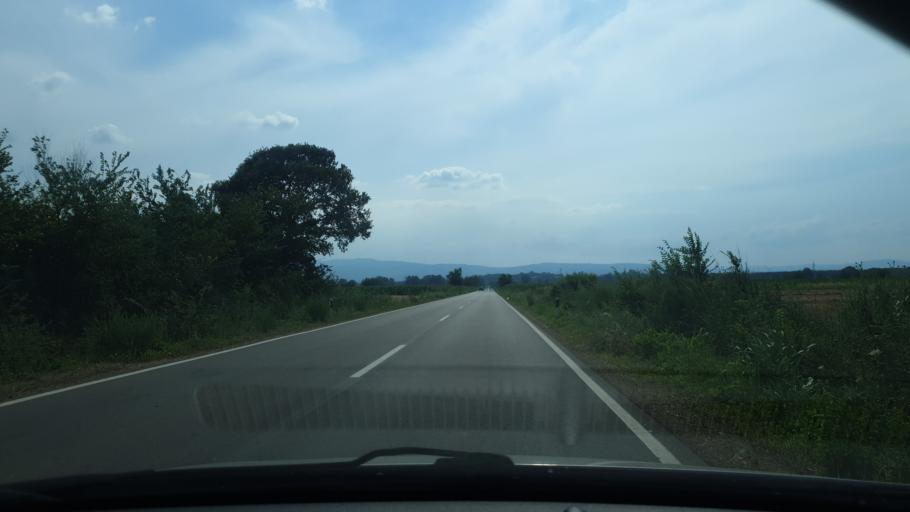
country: RS
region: Central Serbia
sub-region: Pomoravski Okrug
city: Cuprija
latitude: 43.9514
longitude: 21.4422
